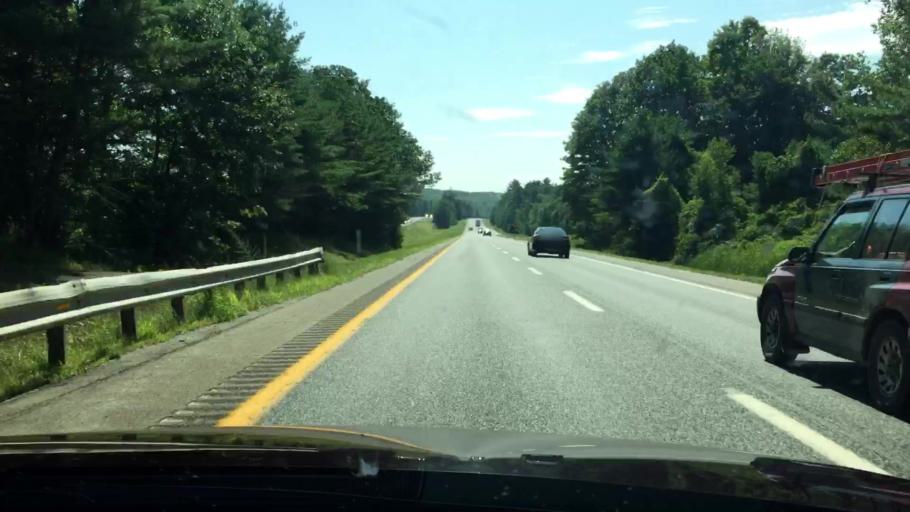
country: US
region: Maine
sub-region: Penobscot County
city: Orono
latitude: 44.8731
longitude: -68.7028
